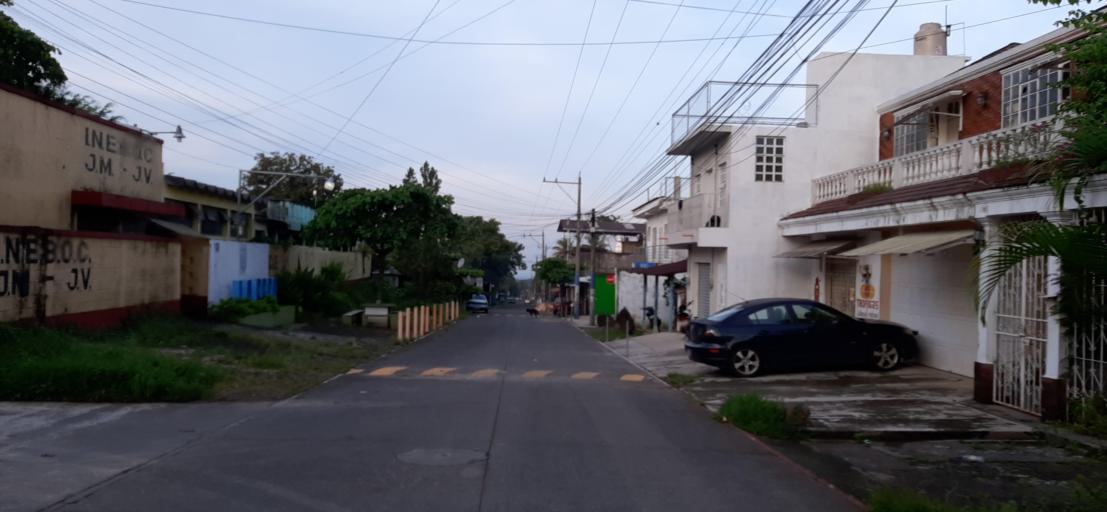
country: GT
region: Retalhuleu
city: San Felipe
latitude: 14.6239
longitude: -91.5999
